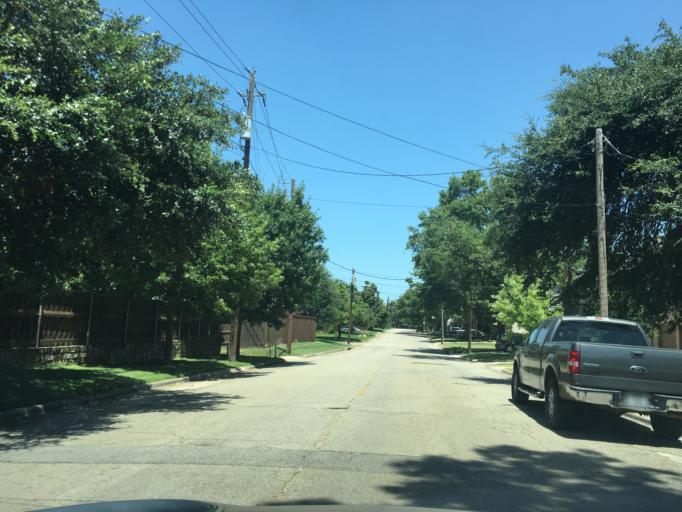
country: US
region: Texas
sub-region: Dallas County
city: Highland Park
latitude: 32.8403
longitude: -96.7384
